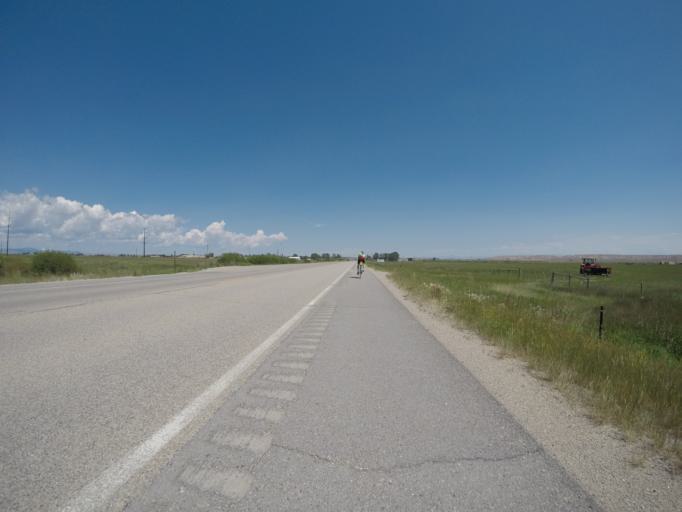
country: US
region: Wyoming
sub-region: Sublette County
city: Marbleton
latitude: 42.5300
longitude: -110.1098
